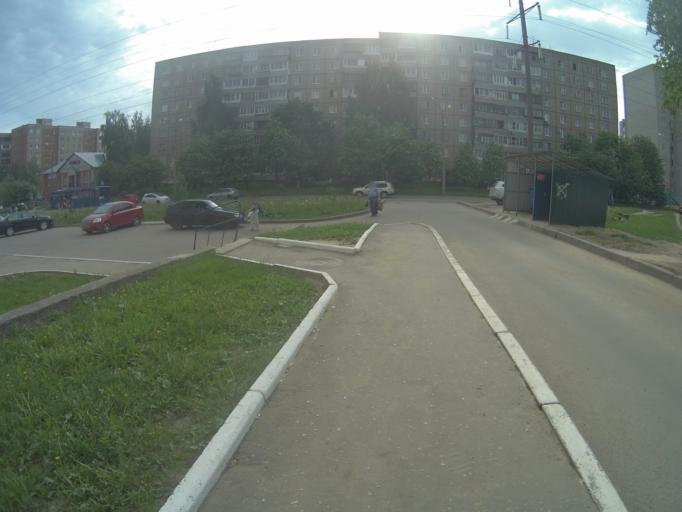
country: RU
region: Vladimir
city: Kommunar
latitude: 56.1638
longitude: 40.4571
